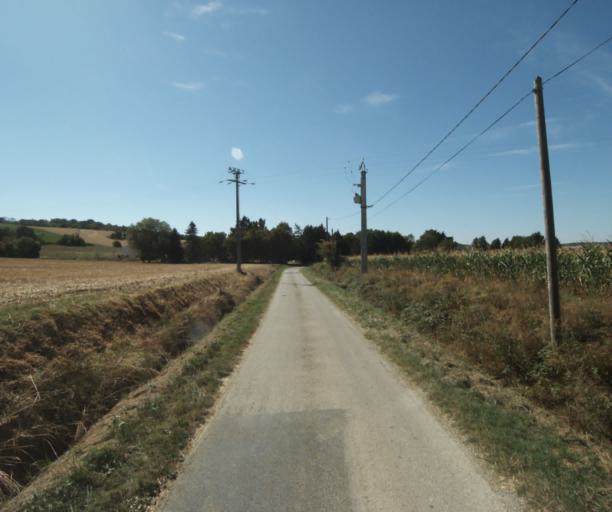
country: FR
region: Midi-Pyrenees
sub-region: Departement de la Haute-Garonne
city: Saint-Felix-Lauragais
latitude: 43.4991
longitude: 1.8989
